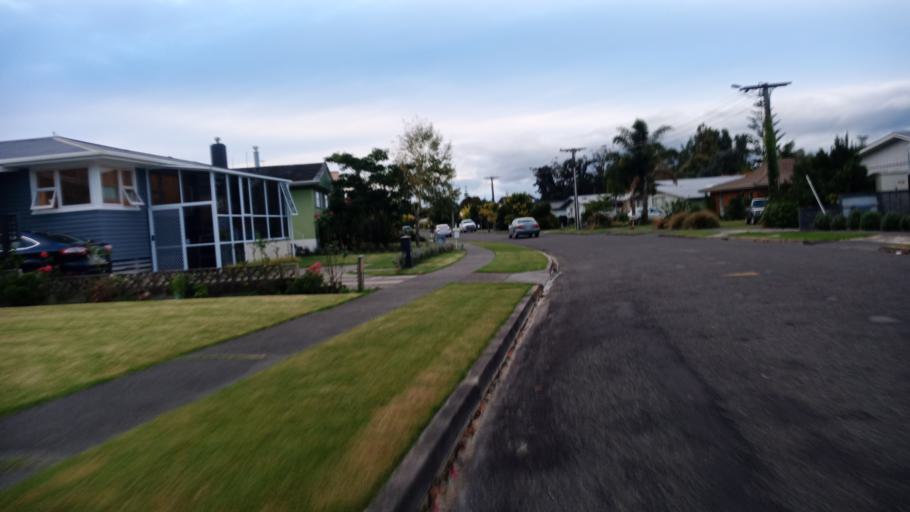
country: NZ
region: Gisborne
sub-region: Gisborne District
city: Gisborne
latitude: -38.6493
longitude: 178.0079
